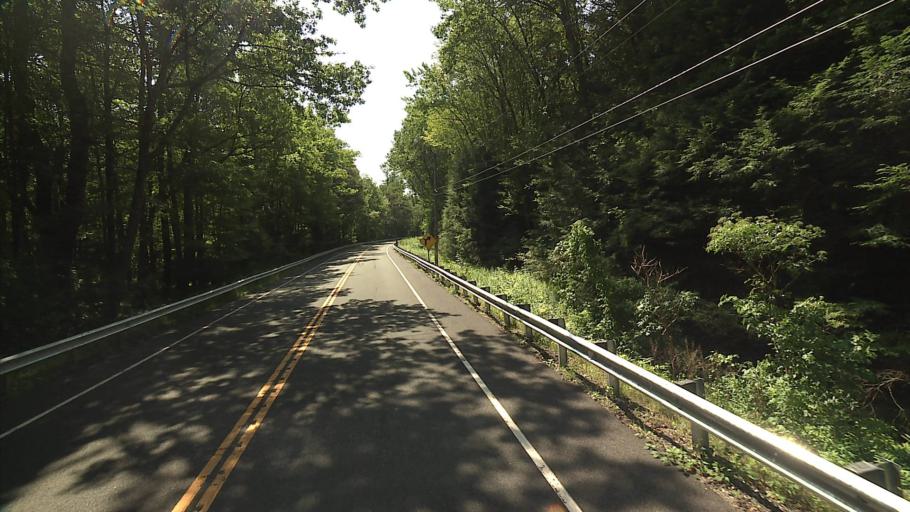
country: US
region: Massachusetts
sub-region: Berkshire County
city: New Marlborough
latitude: 42.0353
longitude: -73.2084
